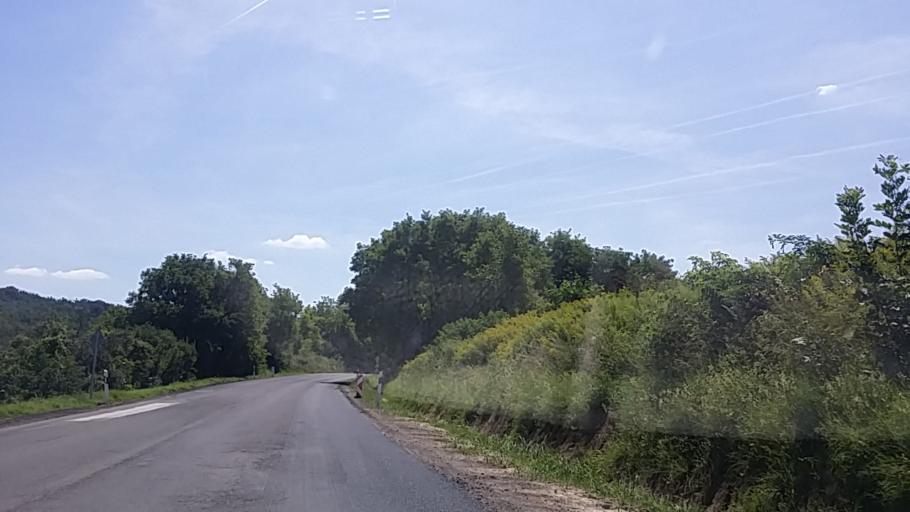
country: HU
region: Somogy
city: Adand
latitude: 46.7857
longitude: 18.1496
